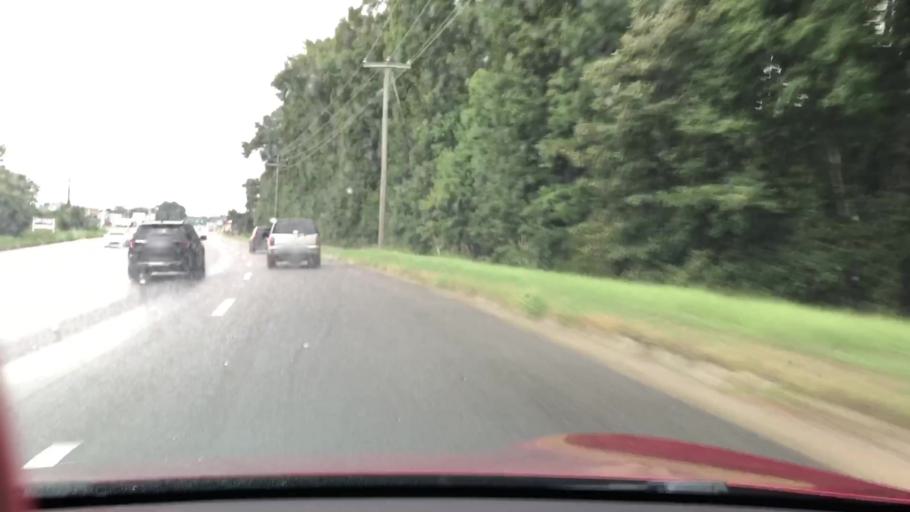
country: US
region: North Carolina
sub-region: Currituck County
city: Moyock
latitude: 36.5441
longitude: -76.1905
